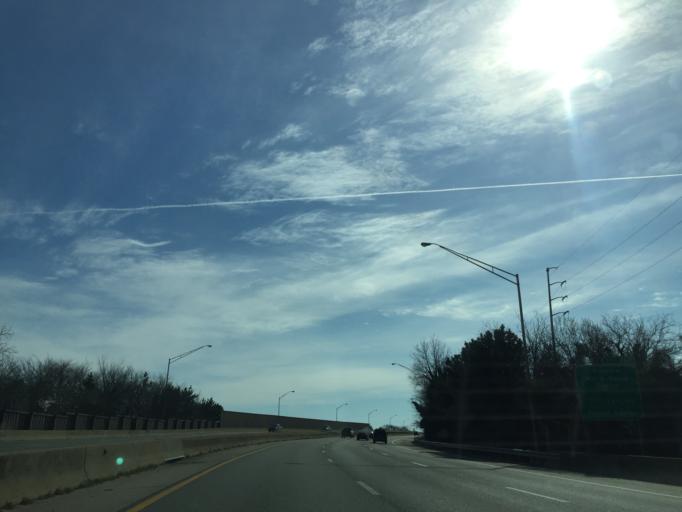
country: US
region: Virginia
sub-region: City of Hampton
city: Hampton
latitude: 37.0332
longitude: -76.3413
